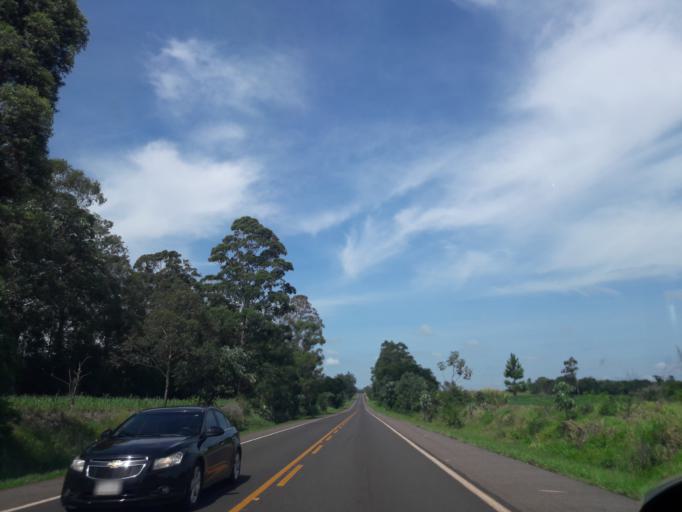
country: BR
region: Parana
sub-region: Campo Mourao
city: Campo Mourao
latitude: -24.2783
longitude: -52.5267
